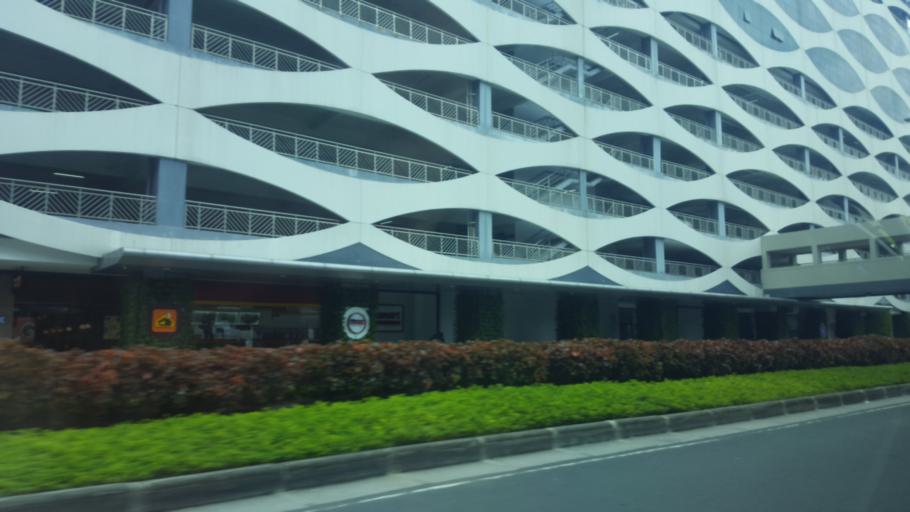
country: PH
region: Metro Manila
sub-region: Makati City
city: Makati City
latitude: 14.5313
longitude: 120.9831
